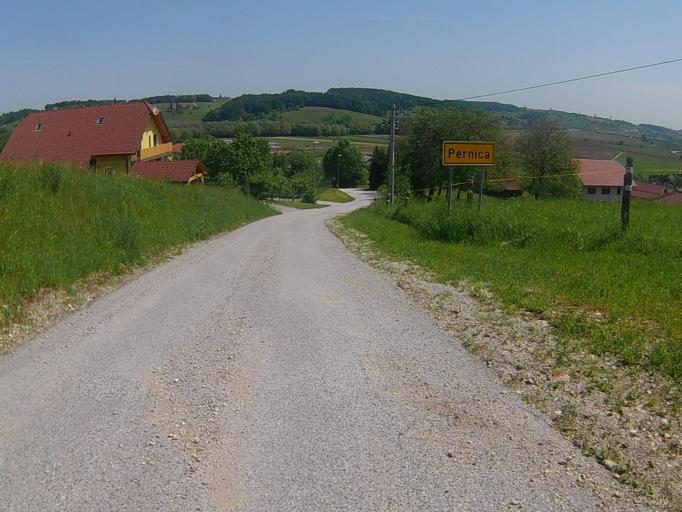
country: SI
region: Pesnica
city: Pesnica pri Mariboru
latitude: 46.5760
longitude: 15.7234
